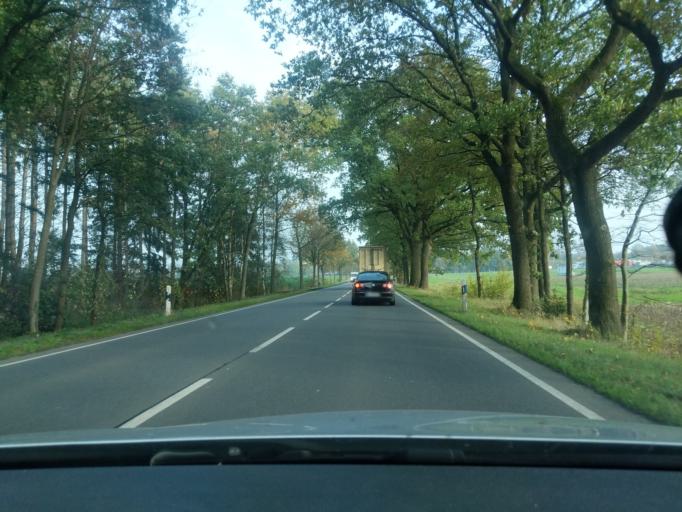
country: DE
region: Lower Saxony
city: Himmelpforten
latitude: 53.6128
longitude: 9.2875
